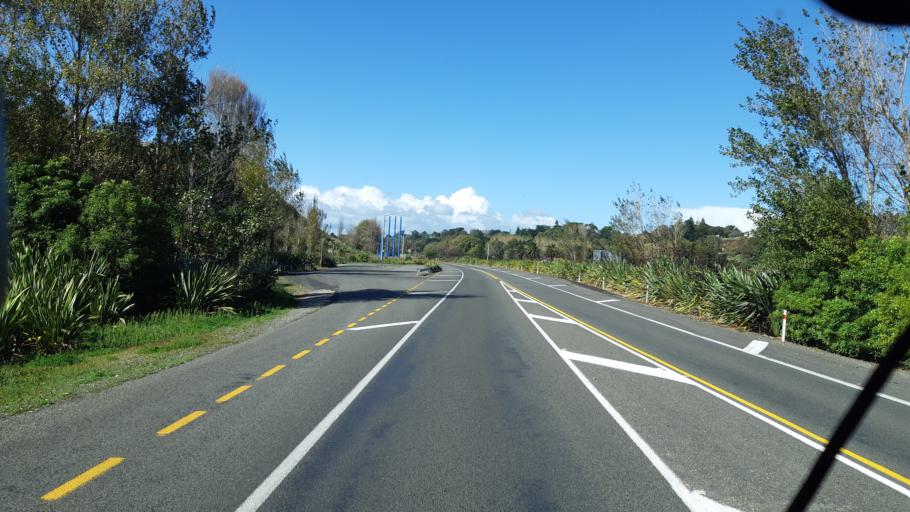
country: NZ
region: Manawatu-Wanganui
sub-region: Wanganui District
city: Wanganui
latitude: -39.9495
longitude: 175.0528
